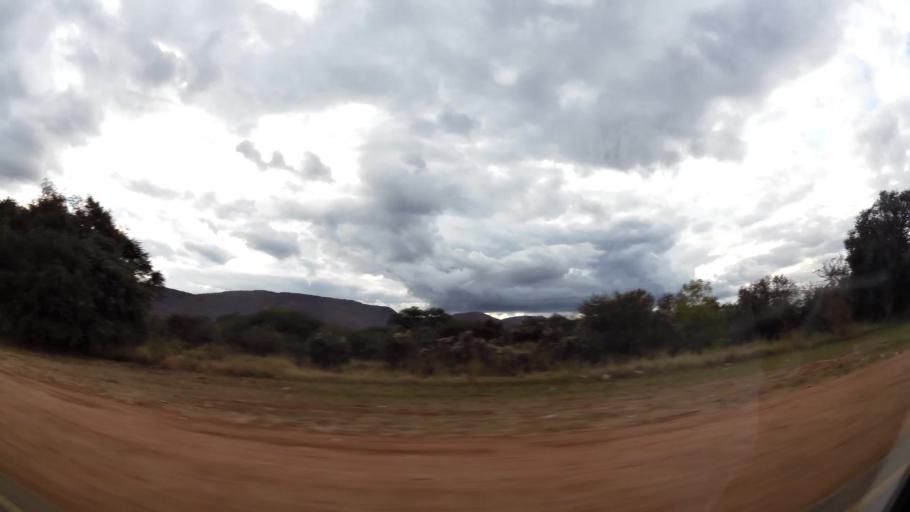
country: ZA
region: Limpopo
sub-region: Waterberg District Municipality
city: Mokopane
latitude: -24.2337
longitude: 28.9979
